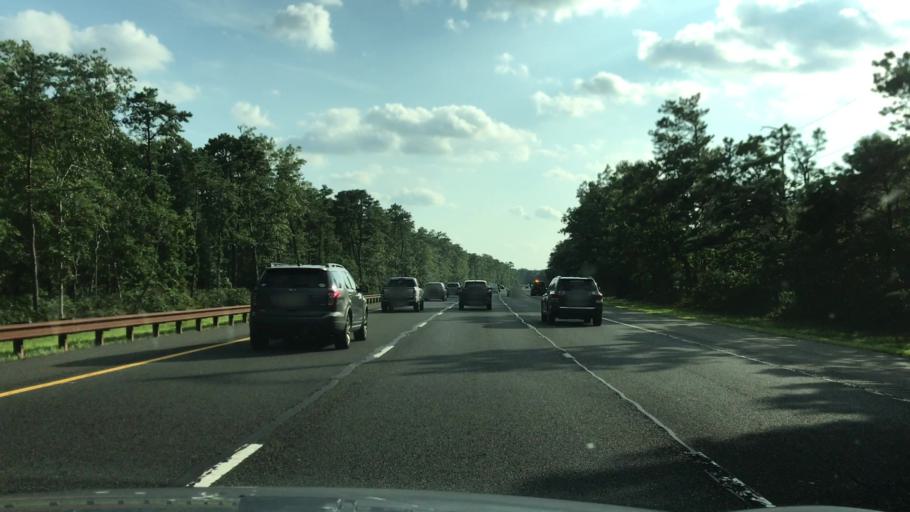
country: US
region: New Jersey
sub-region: Ocean County
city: Tuckerton
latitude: 39.6468
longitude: -74.3574
